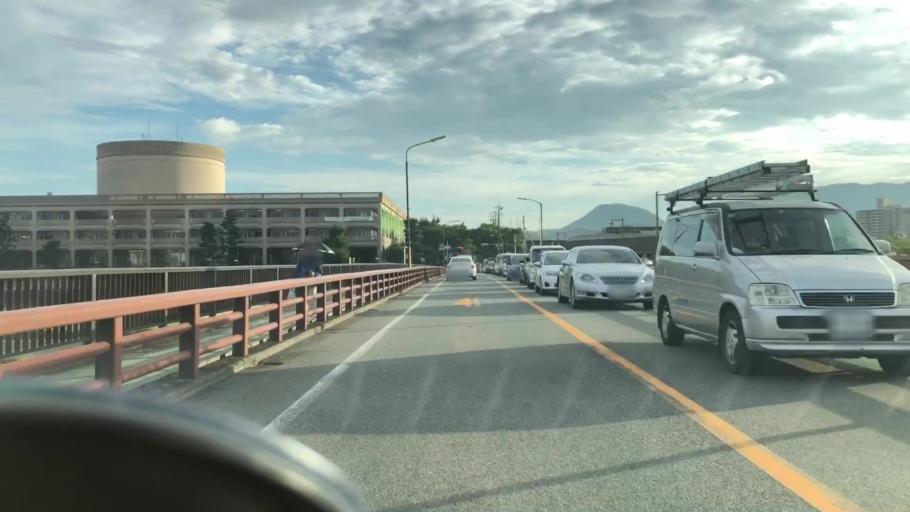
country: JP
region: Hyogo
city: Takarazuka
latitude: 34.8016
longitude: 135.3612
